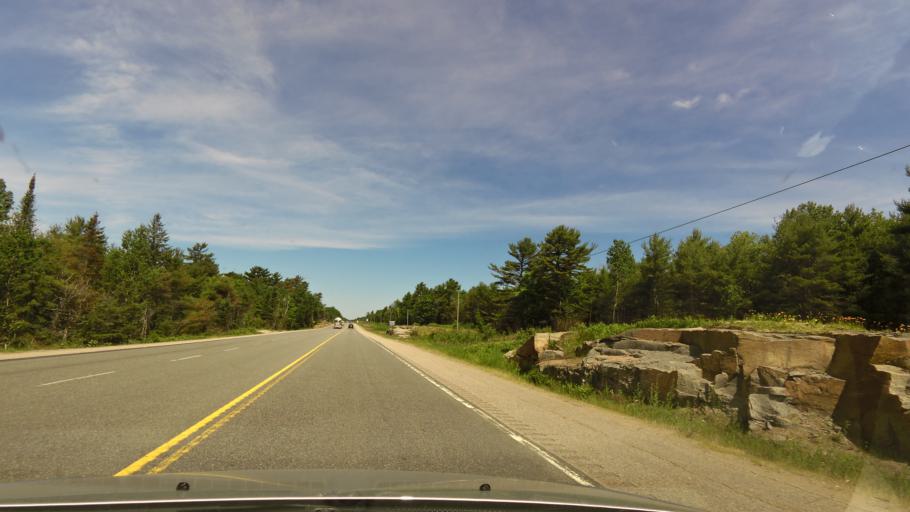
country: CA
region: Ontario
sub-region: Parry Sound District
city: Parry Sound
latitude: 45.5149
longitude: -80.2336
